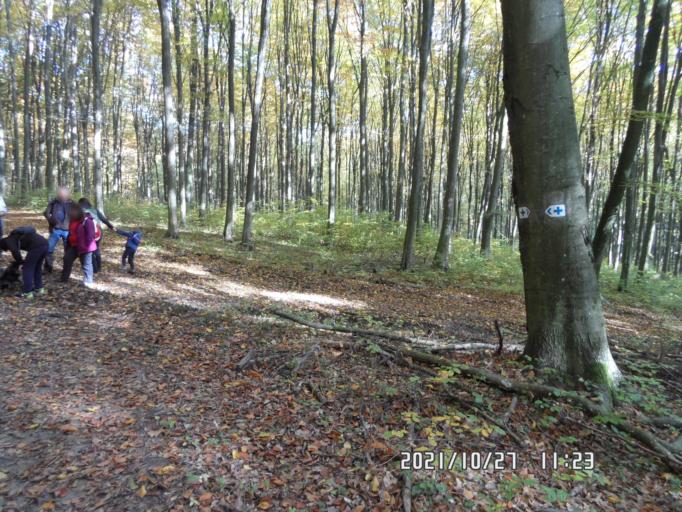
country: HU
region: Zala
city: Letenye
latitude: 46.5099
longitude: 16.7163
